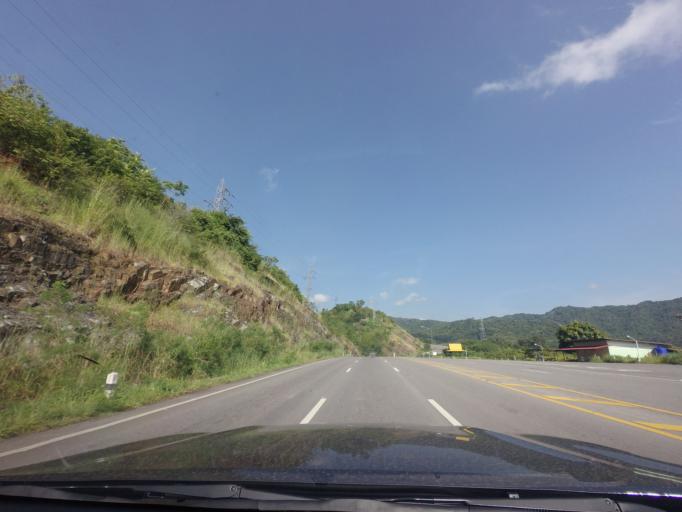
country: TH
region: Phetchabun
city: Lom Sak
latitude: 16.7758
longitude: 101.1196
